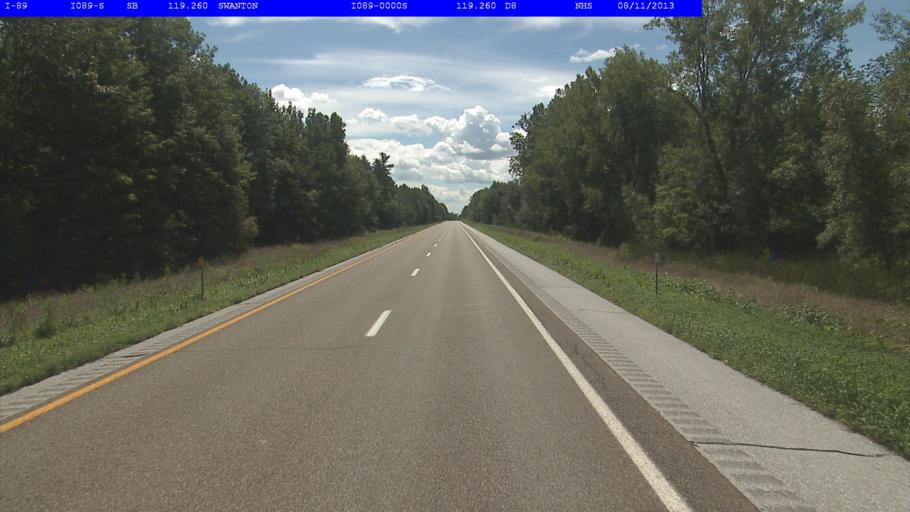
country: US
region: Vermont
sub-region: Franklin County
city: Saint Albans
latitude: 44.8664
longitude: -73.0828
